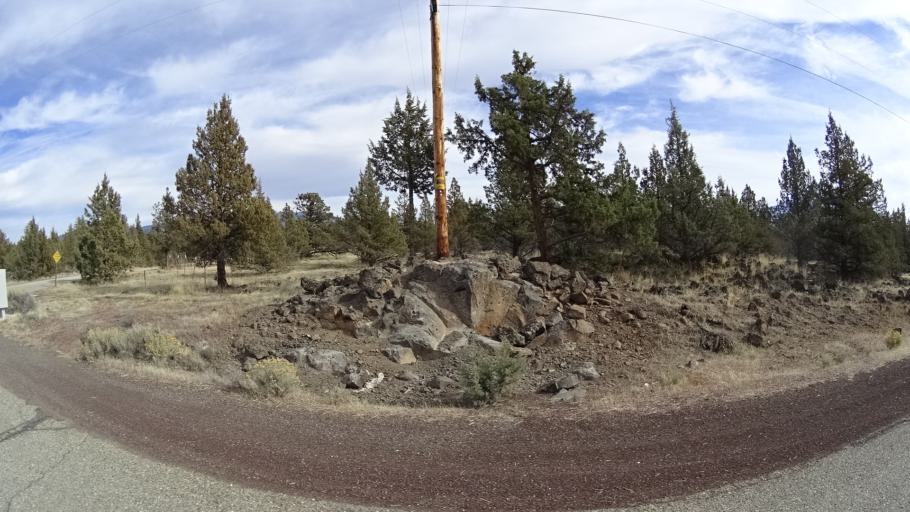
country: US
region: California
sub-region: Siskiyou County
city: Weed
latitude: 41.5954
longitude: -122.3955
